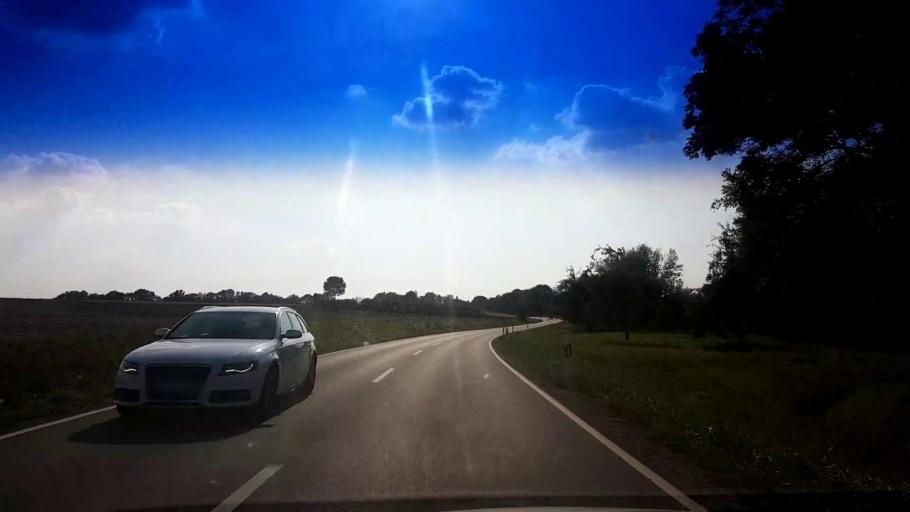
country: DE
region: Bavaria
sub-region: Upper Franconia
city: Schesslitz
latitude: 49.9612
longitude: 11.0104
